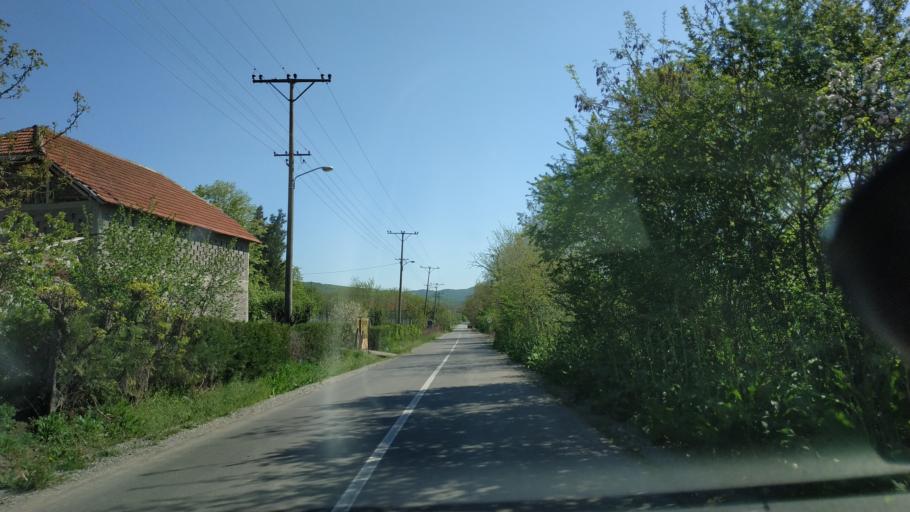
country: RS
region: Central Serbia
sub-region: Nisavski Okrug
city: Nis
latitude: 43.4452
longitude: 21.8472
